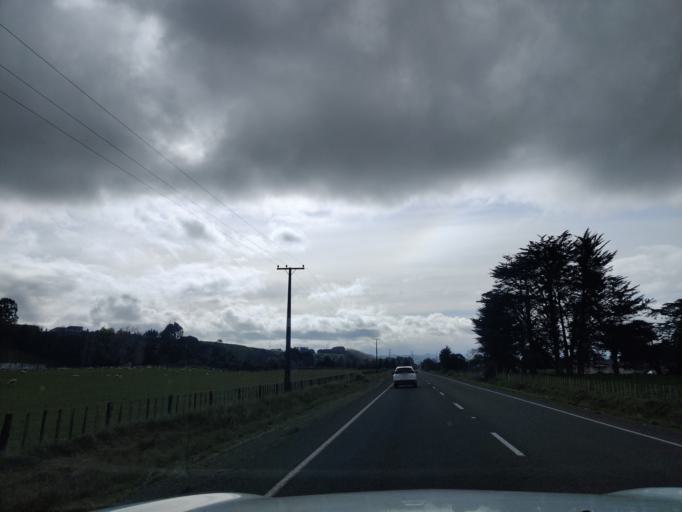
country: NZ
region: Manawatu-Wanganui
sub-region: Rangitikei District
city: Bulls
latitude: -39.8935
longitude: 175.6589
